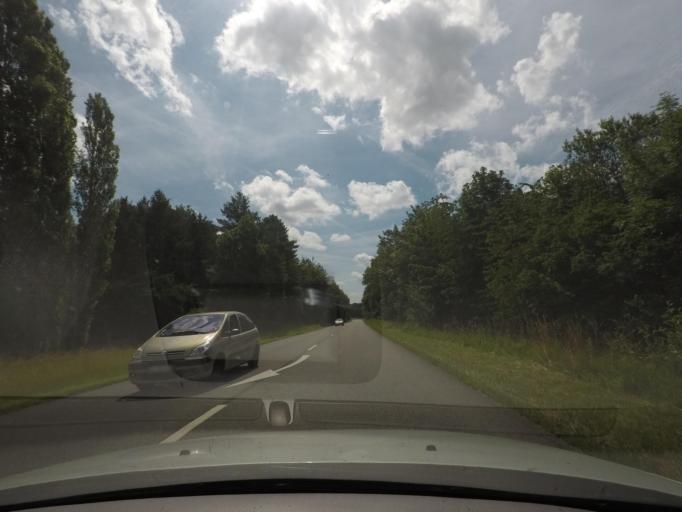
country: FR
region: Alsace
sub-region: Departement du Bas-Rhin
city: Drulingen
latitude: 48.8784
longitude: 7.1560
